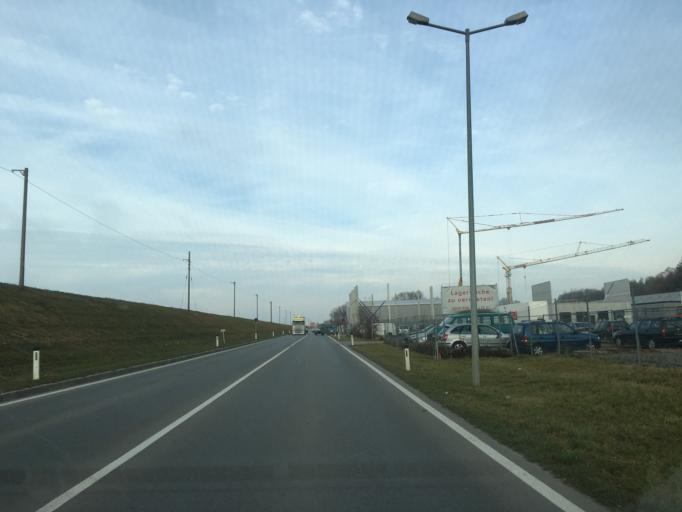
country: AT
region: Vorarlberg
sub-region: Politischer Bezirk Bregenz
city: Fussach
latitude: 47.4739
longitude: 9.6712
